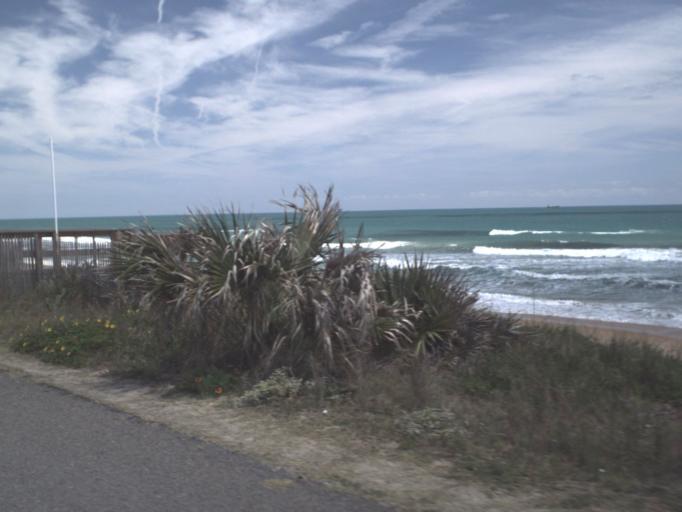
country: US
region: Florida
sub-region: Flagler County
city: Flagler Beach
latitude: 29.4996
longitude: -81.1364
